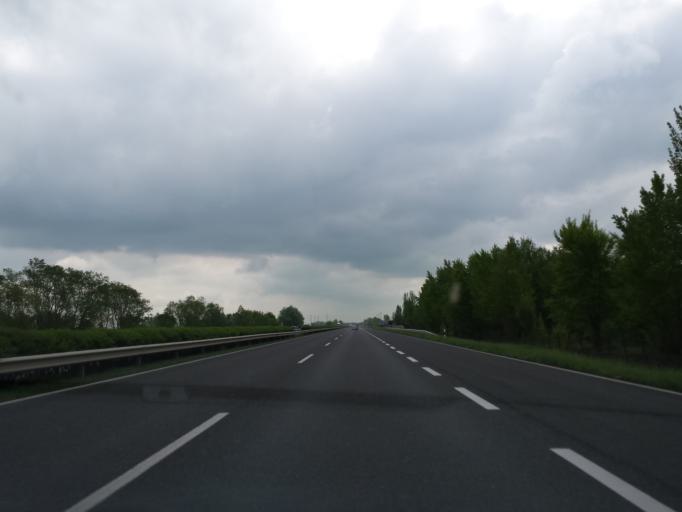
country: HU
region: Gyor-Moson-Sopron
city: Otteveny
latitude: 47.7091
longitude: 17.4843
